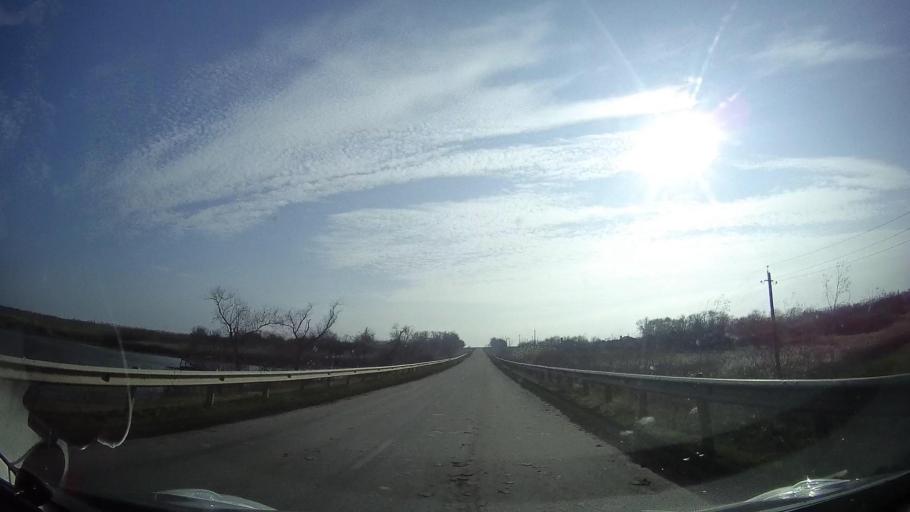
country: RU
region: Rostov
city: Mechetinskaya
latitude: 46.9124
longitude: 40.5355
